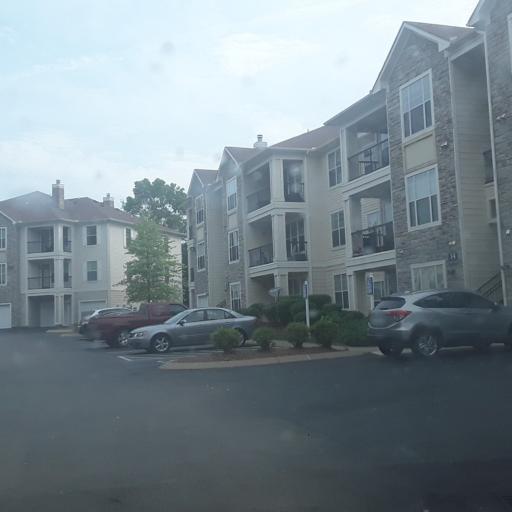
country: US
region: Tennessee
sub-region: Williamson County
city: Brentwood Estates
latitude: 36.0489
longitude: -86.7209
